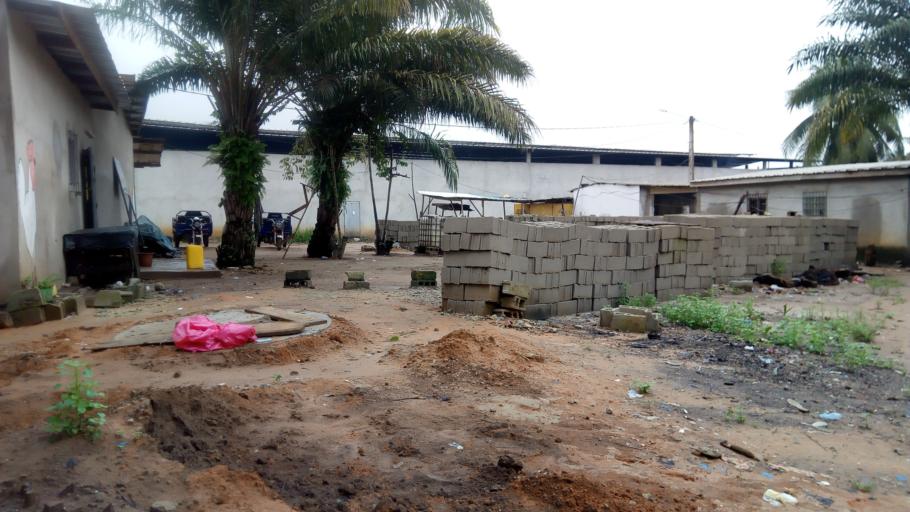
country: CI
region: Lagunes
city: Anyama
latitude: 5.4515
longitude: -4.0720
